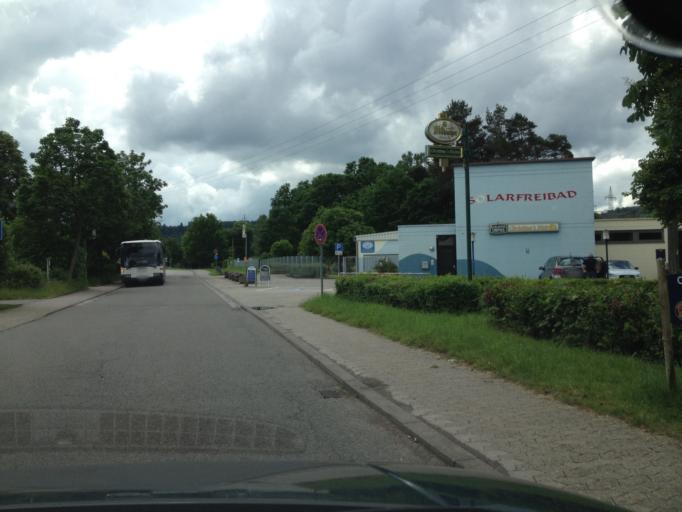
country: DE
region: Saarland
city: Bexbach
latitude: 49.3121
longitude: 7.2662
